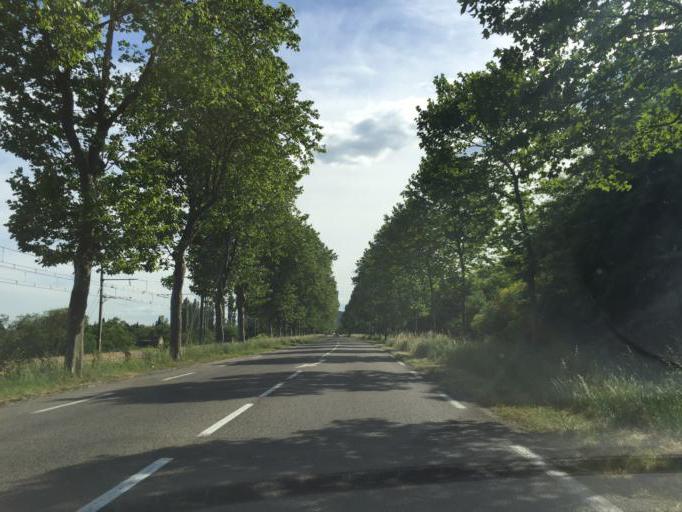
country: FR
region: Rhone-Alpes
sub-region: Departement de l'Ardeche
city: Meysse
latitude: 44.6219
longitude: 4.7392
